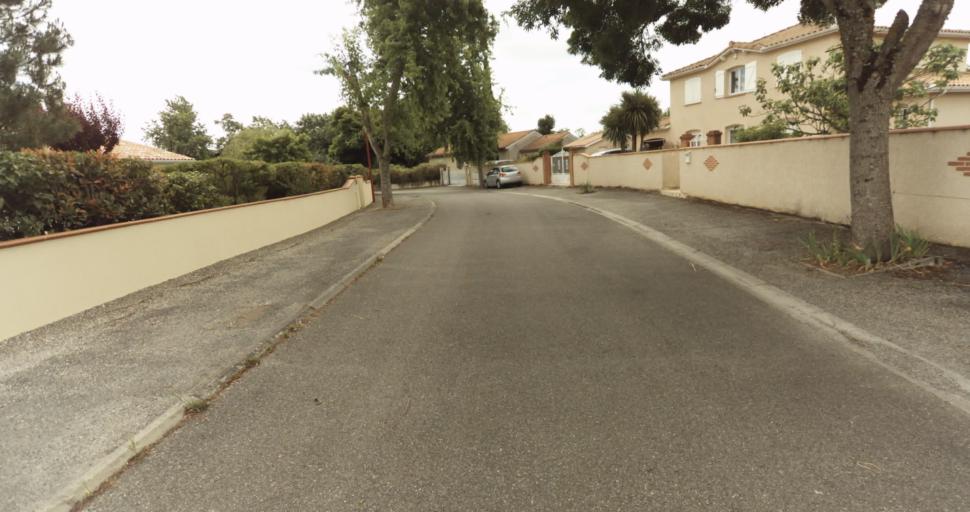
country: FR
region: Midi-Pyrenees
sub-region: Departement de la Haute-Garonne
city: Fontenilles
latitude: 43.5545
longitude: 1.1959
